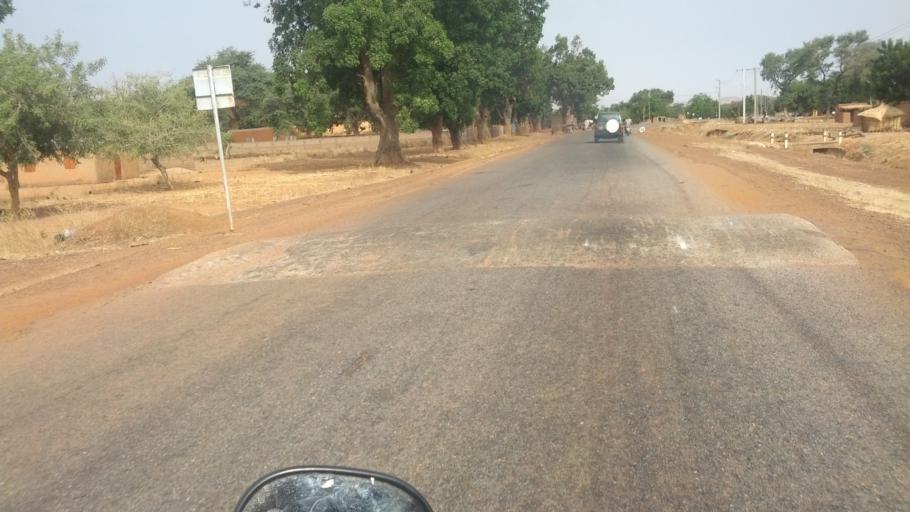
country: BF
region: Centre-Nord
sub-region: Province du Sanmatenga
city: Kaya
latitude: 12.9001
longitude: -1.0779
